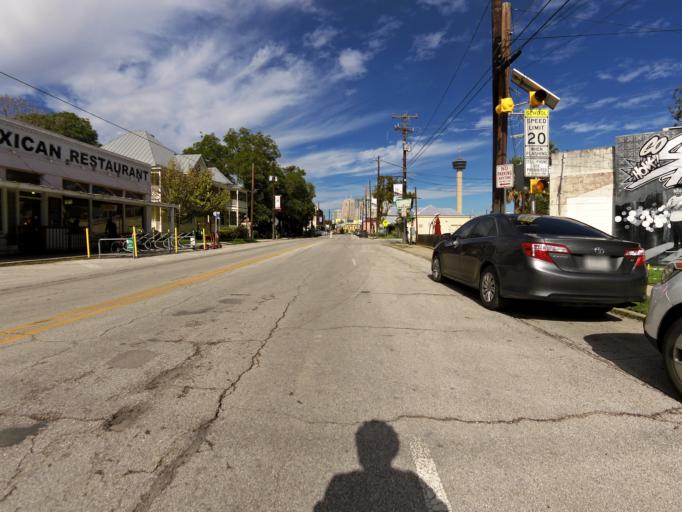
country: US
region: Texas
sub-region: Bexar County
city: San Antonio
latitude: 29.4139
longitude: -98.4909
